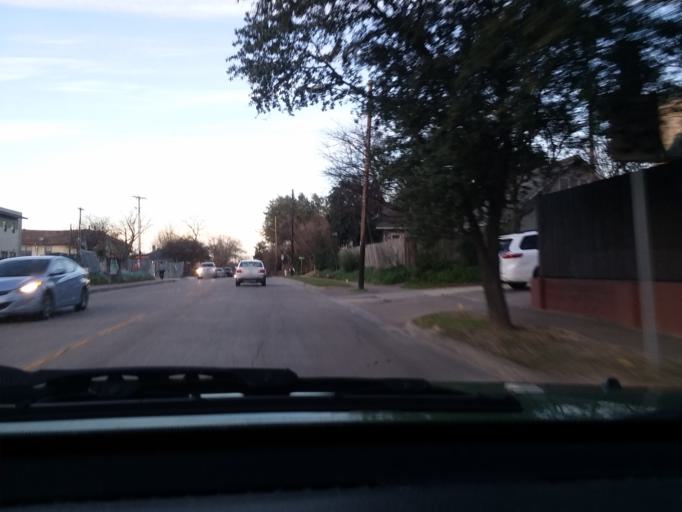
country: US
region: Texas
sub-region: Dallas County
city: Highland Park
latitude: 32.8179
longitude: -96.7702
